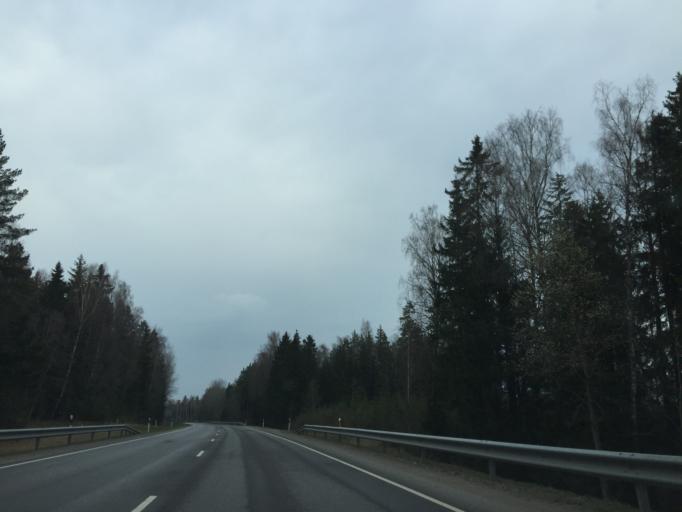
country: EE
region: Tartu
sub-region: UElenurme vald
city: Ulenurme
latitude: 58.1016
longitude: 26.7404
